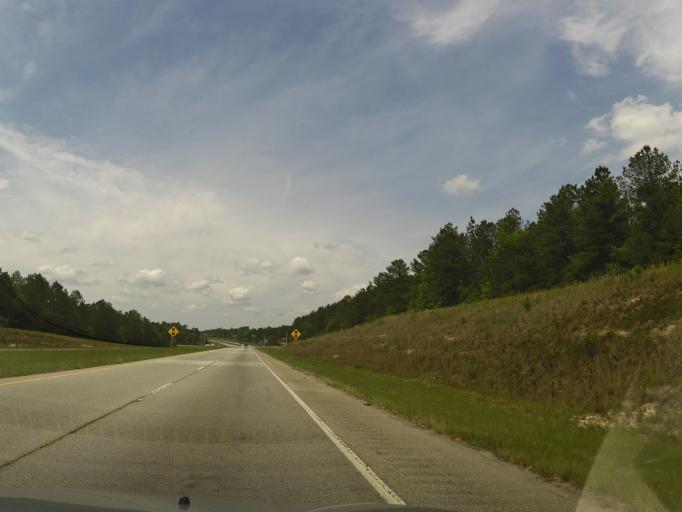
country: US
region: Georgia
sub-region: Emanuel County
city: Swainsboro
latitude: 32.5829
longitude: -82.3640
